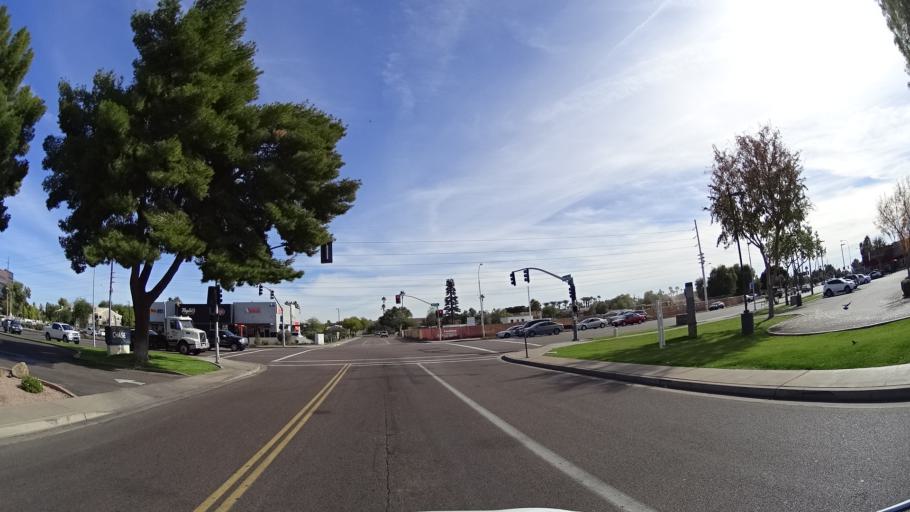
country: US
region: Arizona
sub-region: Maricopa County
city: Guadalupe
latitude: 33.3800
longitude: -111.9288
